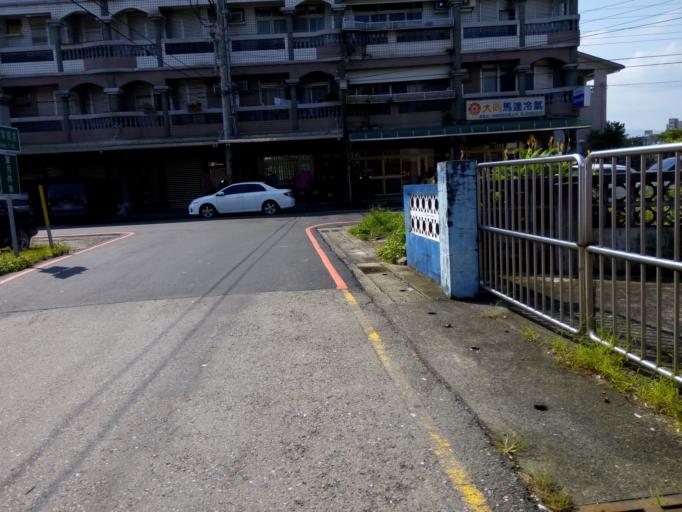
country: TW
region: Taiwan
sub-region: Yilan
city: Yilan
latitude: 24.6709
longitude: 121.7813
